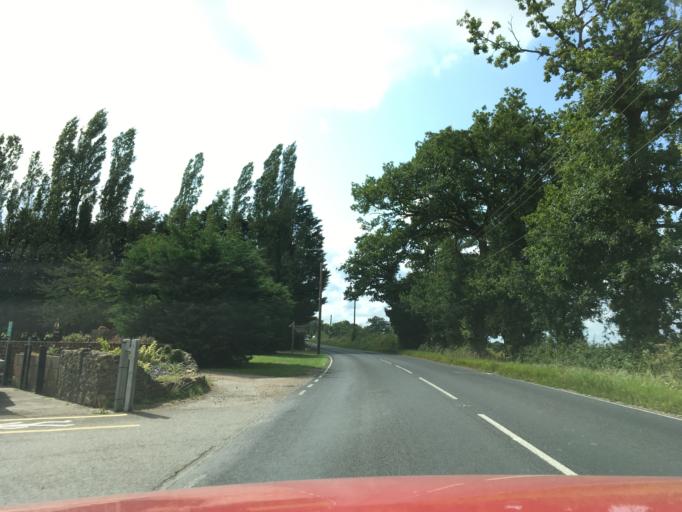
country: GB
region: England
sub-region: Kent
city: Tenterden
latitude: 51.1042
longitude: 0.6510
